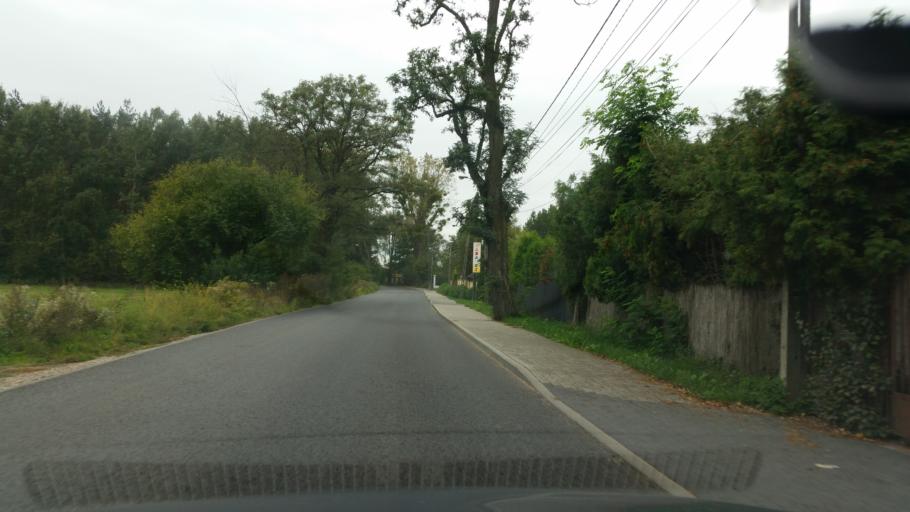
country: PL
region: Masovian Voivodeship
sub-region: Warszawa
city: Kabaty
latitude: 52.1026
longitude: 21.0861
